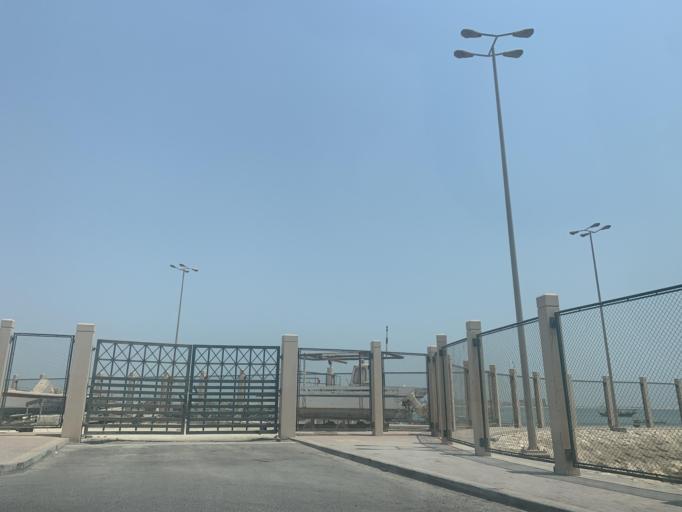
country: BH
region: Muharraq
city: Al Hadd
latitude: 26.2449
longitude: 50.6595
